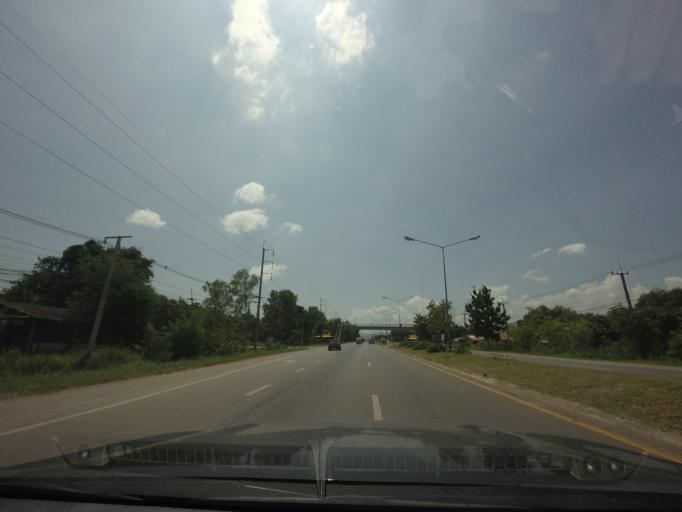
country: TH
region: Phetchabun
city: Lom Sak
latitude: 16.7019
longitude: 101.1734
